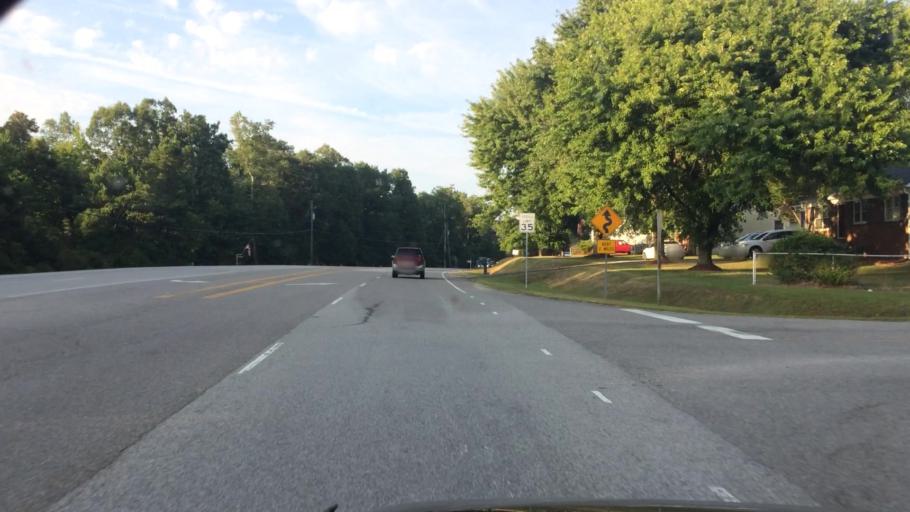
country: US
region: Virginia
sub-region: James City County
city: Williamsburg
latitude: 37.3304
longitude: -76.7347
